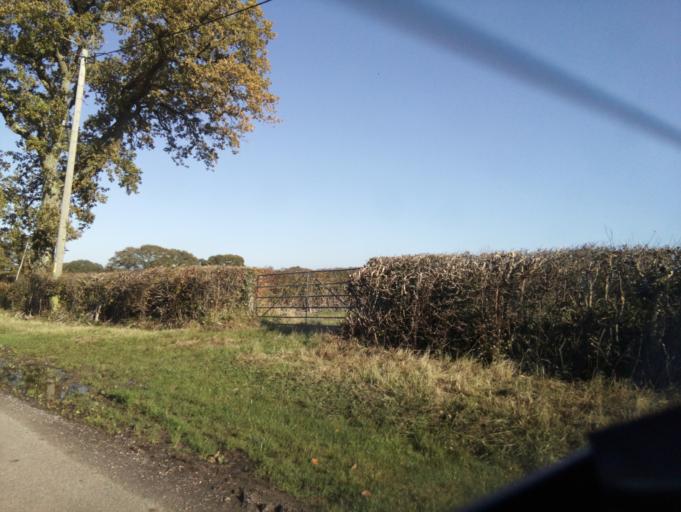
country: GB
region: England
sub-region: Somerset
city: Yeovil
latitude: 50.8845
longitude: -2.5954
